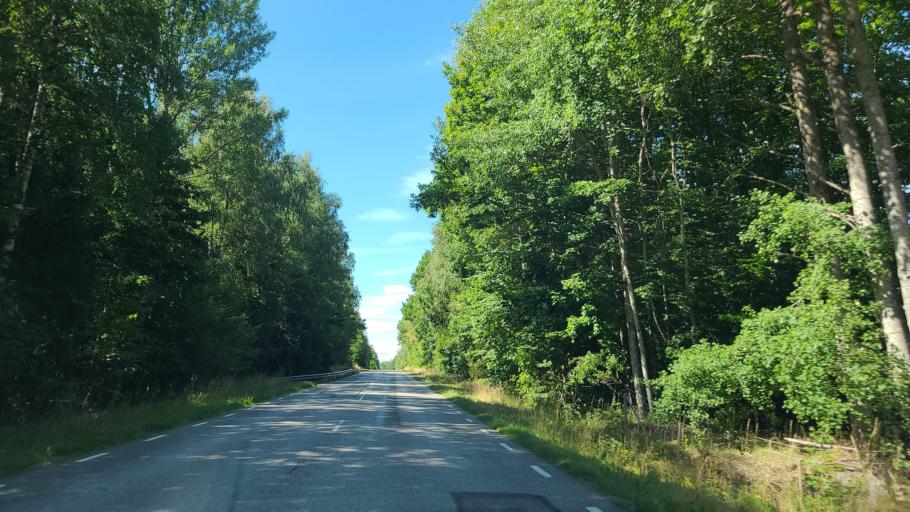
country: SE
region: Kalmar
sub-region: Emmaboda Kommun
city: Emmaboda
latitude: 56.5521
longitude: 15.7070
